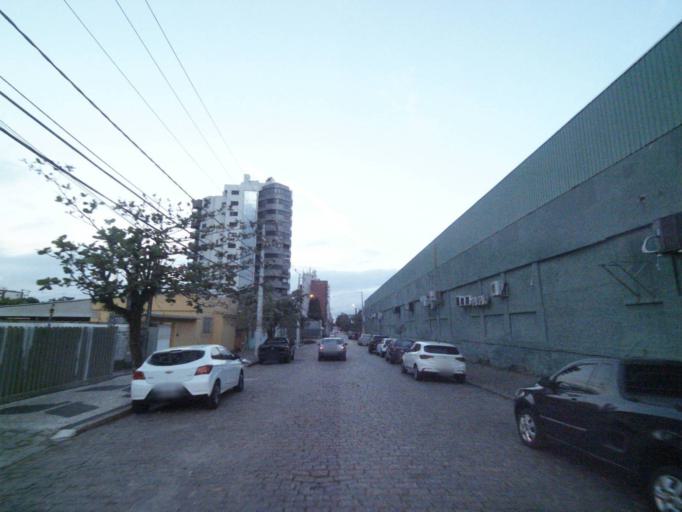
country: BR
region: Parana
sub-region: Paranagua
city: Paranagua
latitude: -25.5150
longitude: -48.5072
